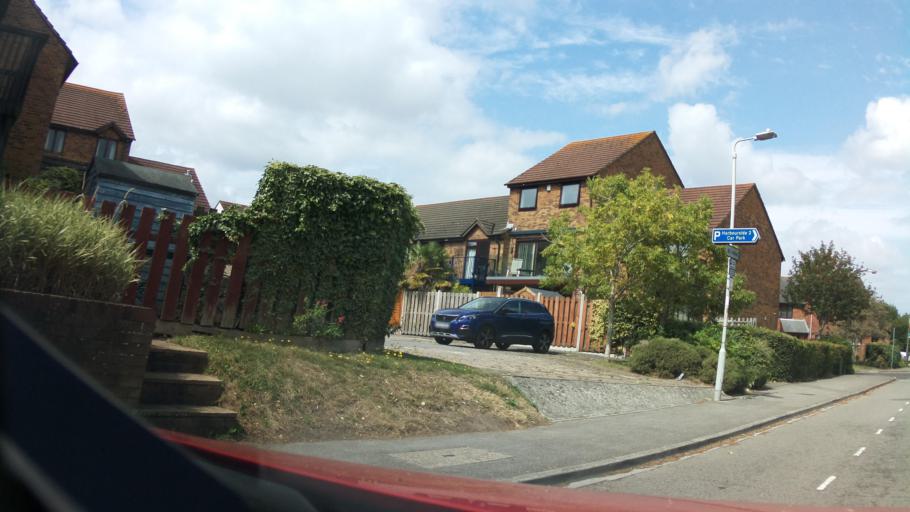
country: GB
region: England
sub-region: Poole
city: Poole
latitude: 50.7131
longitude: -1.9728
